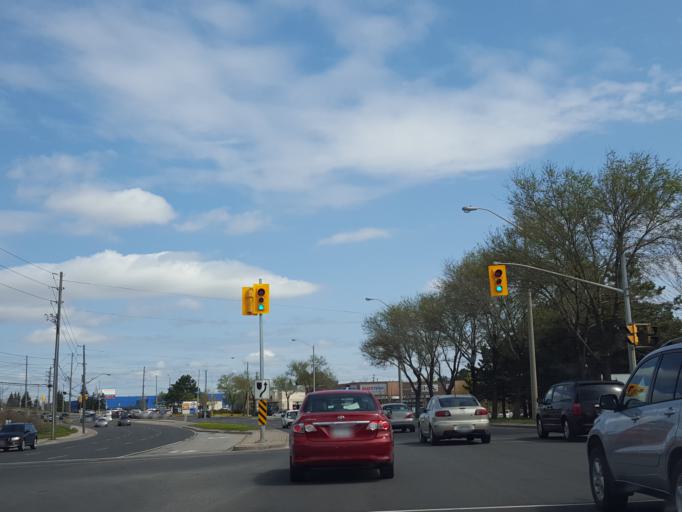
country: CA
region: Ontario
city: Scarborough
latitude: 43.8106
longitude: -79.2429
